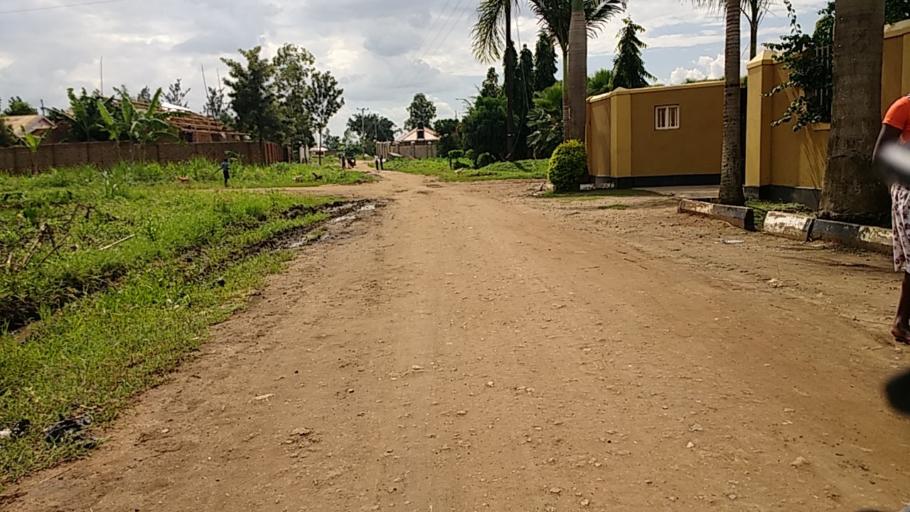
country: UG
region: Eastern Region
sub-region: Mbale District
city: Mbale
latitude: 1.0881
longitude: 34.1721
